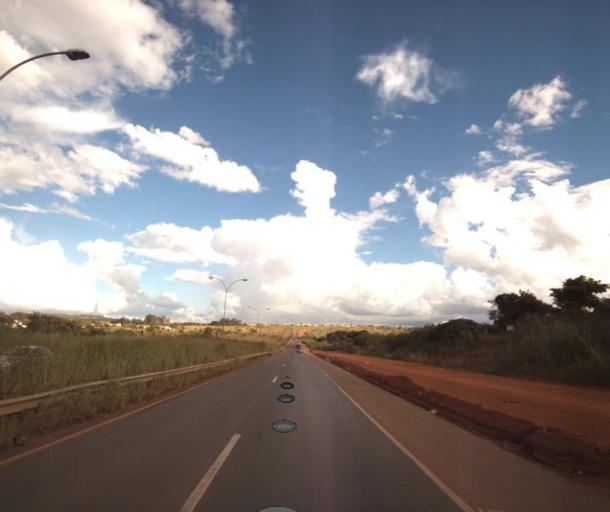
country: BR
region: Goias
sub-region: Anapolis
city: Anapolis
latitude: -16.3045
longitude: -48.9248
